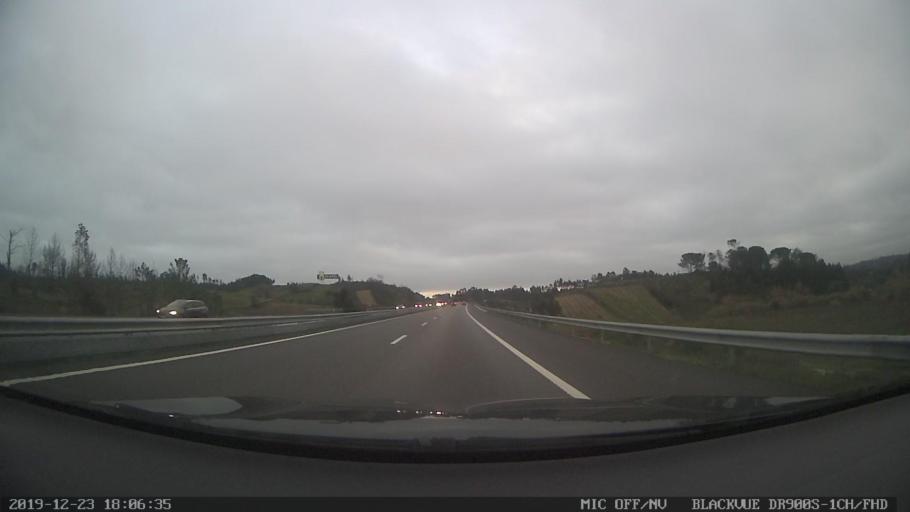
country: PT
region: Aveiro
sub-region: Mealhada
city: Pampilhosa do Botao
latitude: 40.3011
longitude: -8.4861
